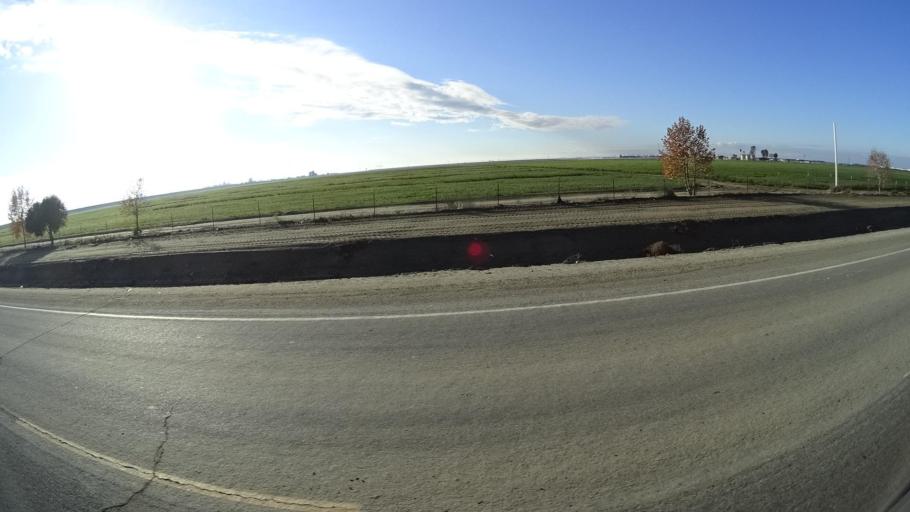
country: US
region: California
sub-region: Kern County
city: Delano
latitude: 35.7762
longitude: -119.2976
